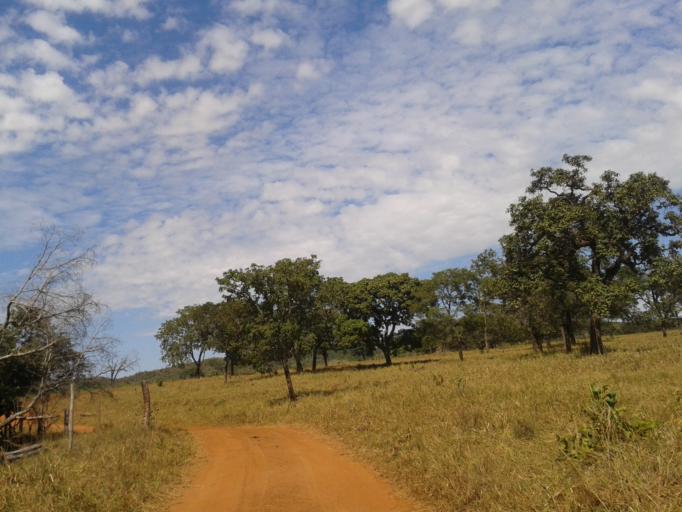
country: BR
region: Minas Gerais
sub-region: Campina Verde
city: Campina Verde
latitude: -19.3950
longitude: -49.7668
